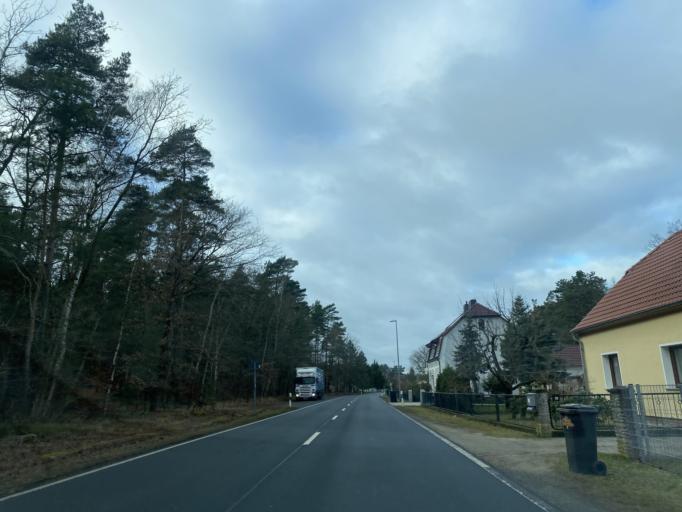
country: PL
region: Lubusz
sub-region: Powiat zarski
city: Przewoz
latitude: 51.4807
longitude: 14.8554
